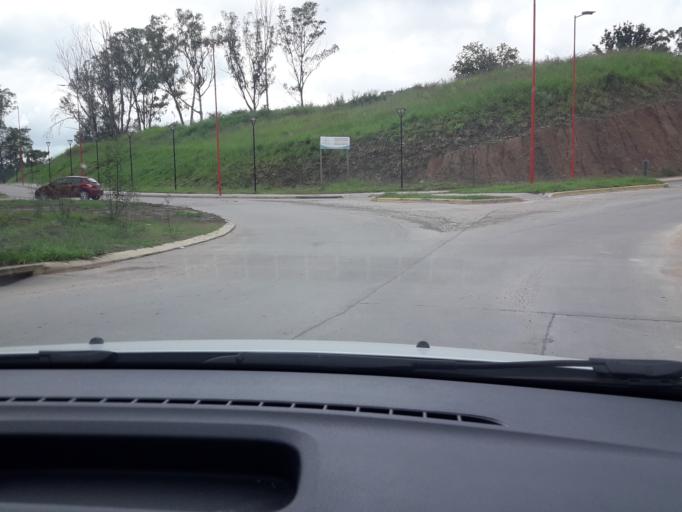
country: AR
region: Jujuy
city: San Salvador de Jujuy
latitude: -24.1794
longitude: -65.3269
